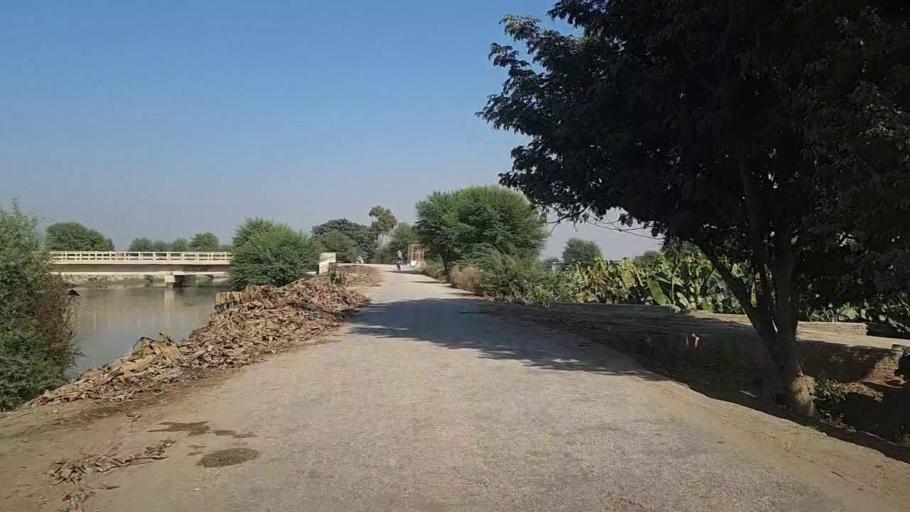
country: PK
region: Sindh
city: Bozdar
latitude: 27.2045
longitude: 68.6673
